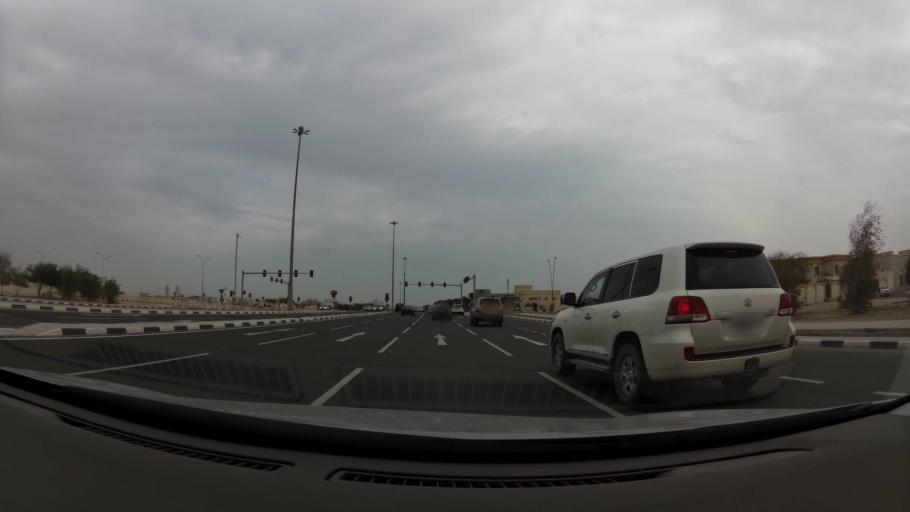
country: QA
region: Baladiyat ad Dawhah
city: Doha
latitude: 25.3485
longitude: 51.4876
